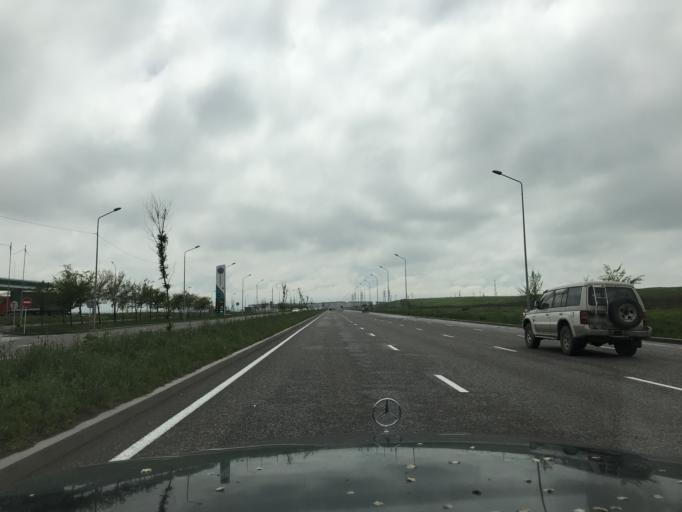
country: KZ
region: Almaty Oblysy
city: Burunday
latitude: 43.2963
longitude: 76.8329
